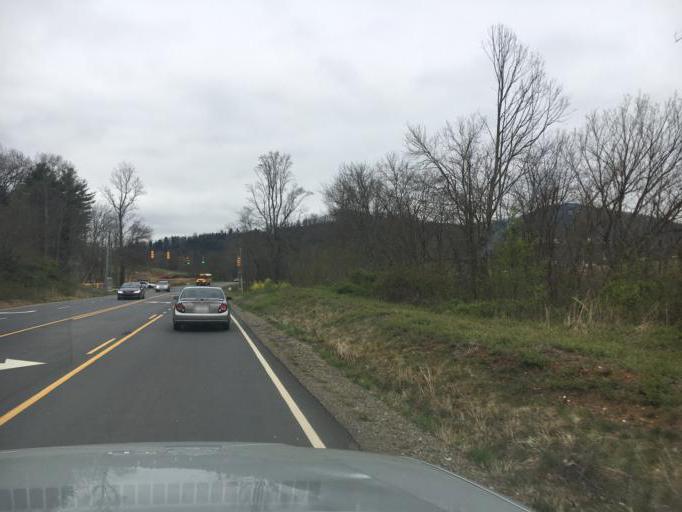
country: US
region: North Carolina
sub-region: Buncombe County
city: Woodfin
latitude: 35.6181
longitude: -82.6234
